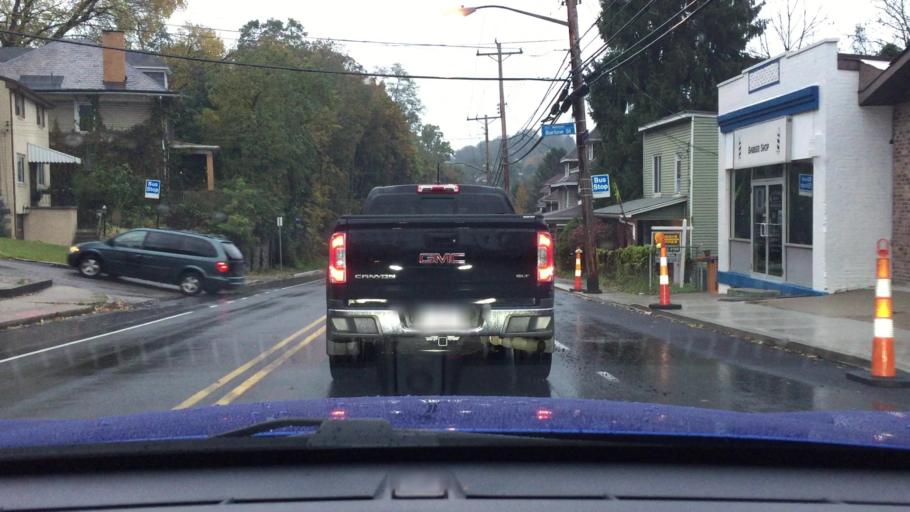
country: US
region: Pennsylvania
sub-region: Allegheny County
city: Crafton
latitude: 40.4361
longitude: -80.0519
